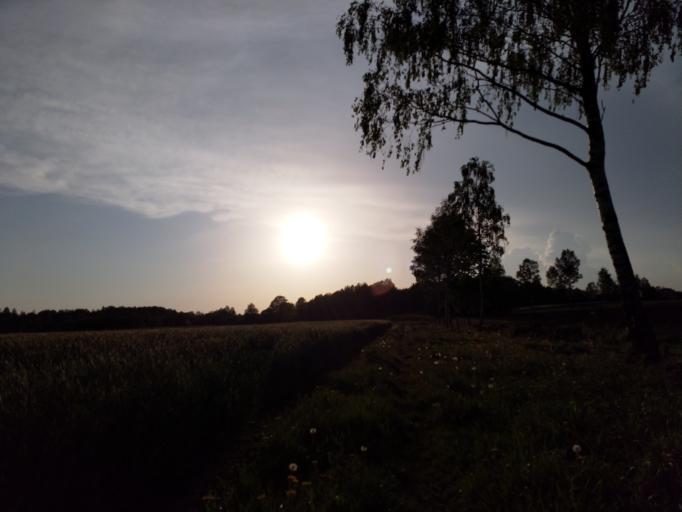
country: LV
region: Aizpute
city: Aizpute
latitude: 56.8284
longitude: 21.7841
